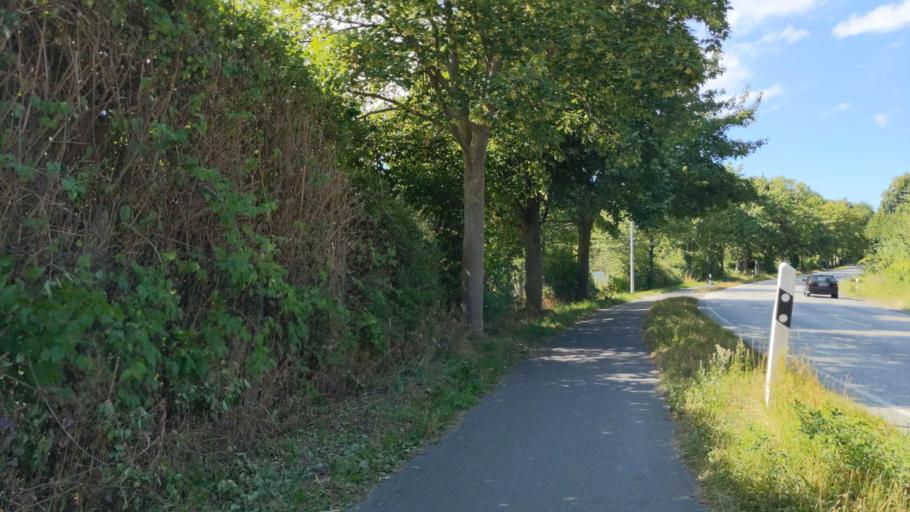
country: DE
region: Schleswig-Holstein
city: Dornick
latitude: 54.1491
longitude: 10.3930
